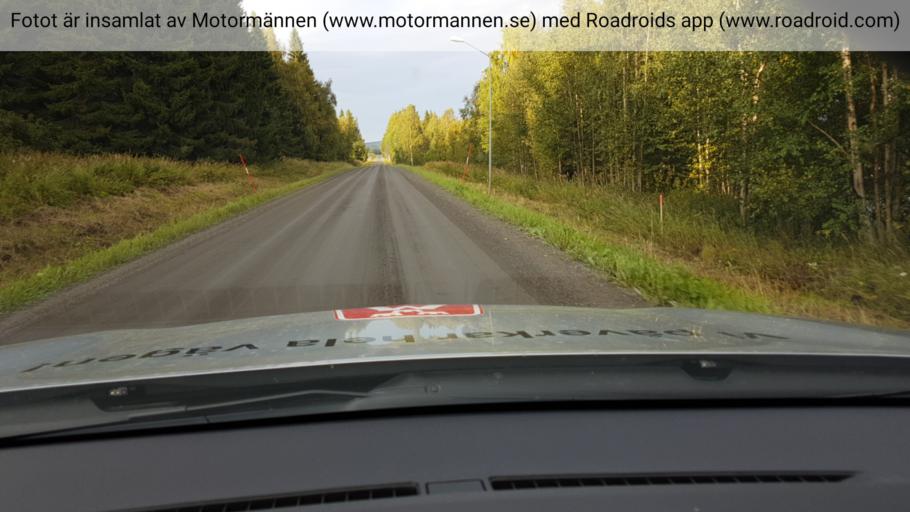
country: SE
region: Jaemtland
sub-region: Stroemsunds Kommun
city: Stroemsund
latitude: 64.0412
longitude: 15.8100
